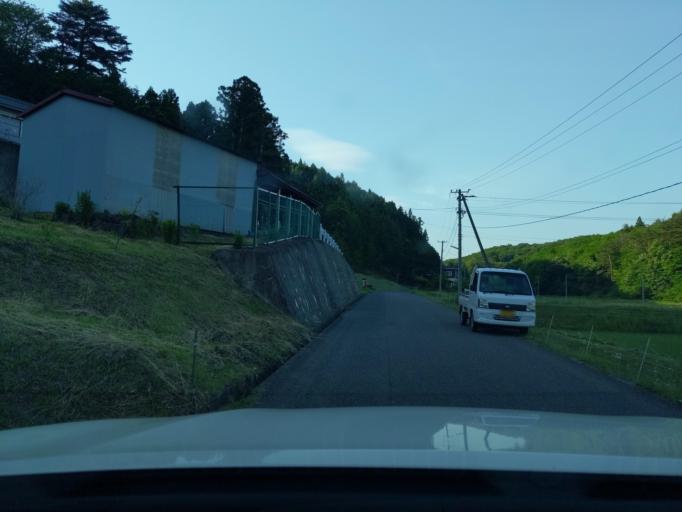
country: JP
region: Fukushima
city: Motomiya
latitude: 37.5208
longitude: 140.3313
